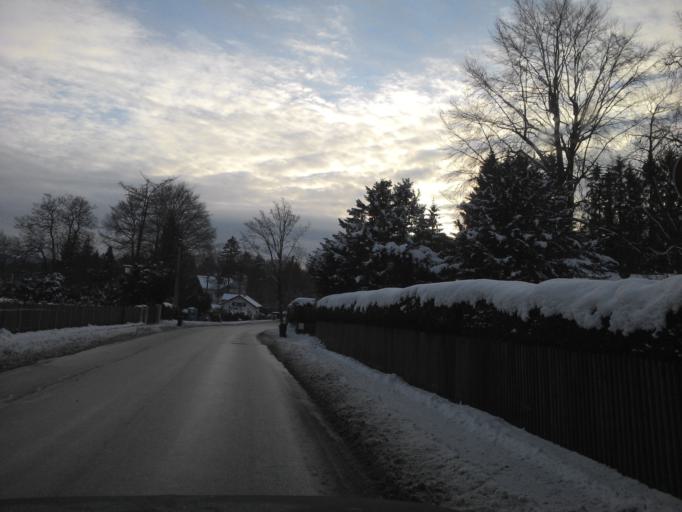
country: DE
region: Bavaria
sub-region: Upper Bavaria
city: Seeshaupt
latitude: 47.8213
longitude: 11.3118
